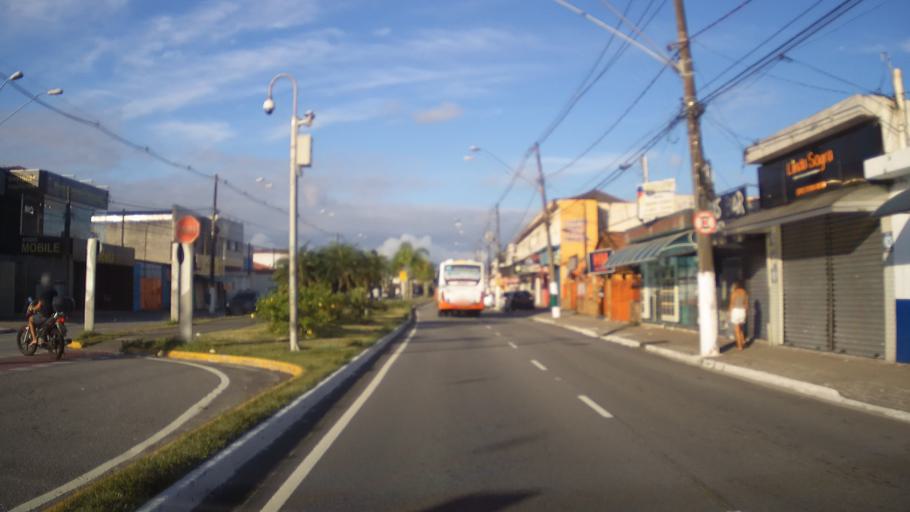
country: BR
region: Sao Paulo
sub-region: Praia Grande
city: Praia Grande
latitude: -24.0135
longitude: -46.4459
